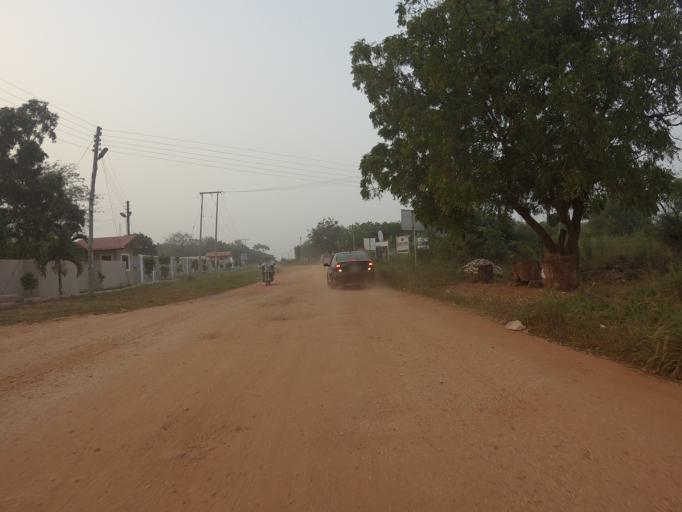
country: GH
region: Volta
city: Anloga
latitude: 5.9935
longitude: 0.5926
